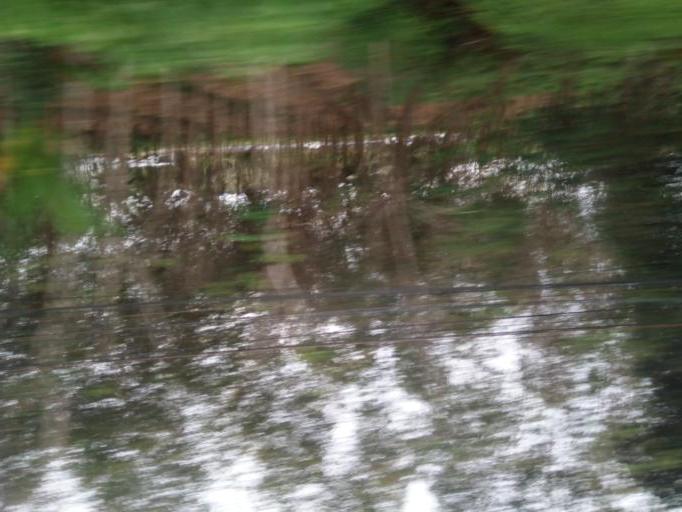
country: TH
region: Phuket
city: Thalang
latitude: 8.0593
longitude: 98.4026
